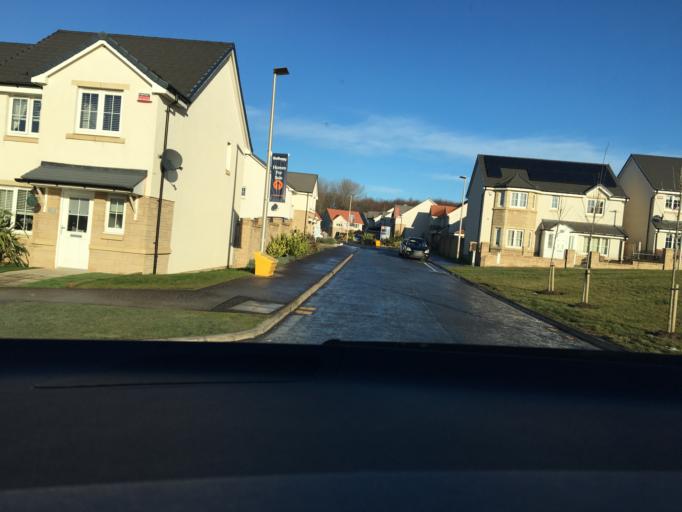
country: GB
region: Scotland
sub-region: Midlothian
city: Dalkeith
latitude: 55.8981
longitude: -3.0404
